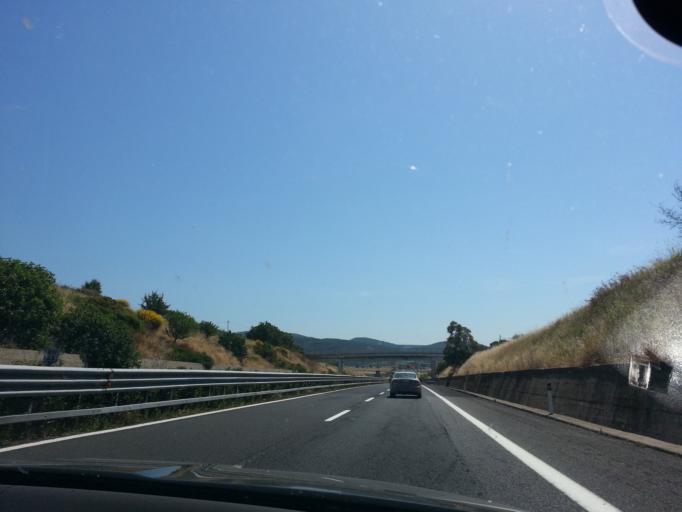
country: IT
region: Latium
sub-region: Citta metropolitana di Roma Capitale
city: Santa Marinella
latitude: 42.0437
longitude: 11.9117
